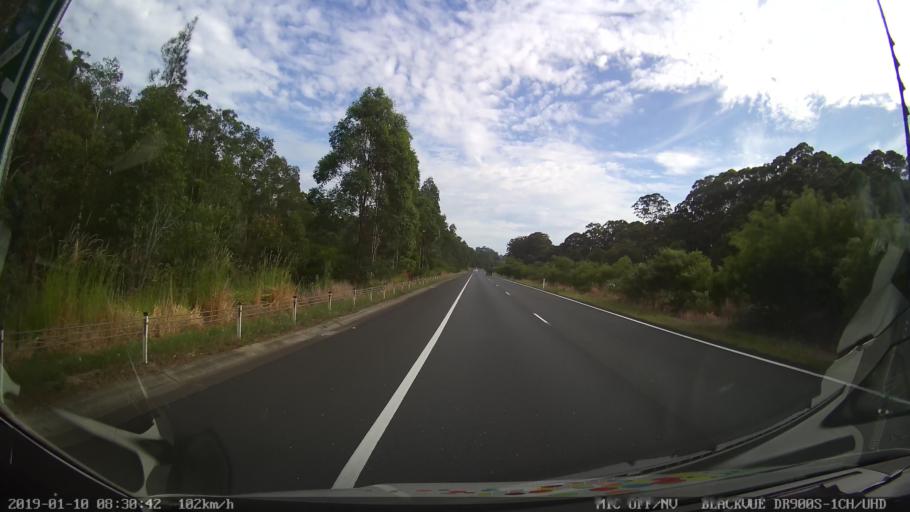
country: AU
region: New South Wales
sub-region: Coffs Harbour
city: Bonville
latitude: -30.3661
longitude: 153.0550
